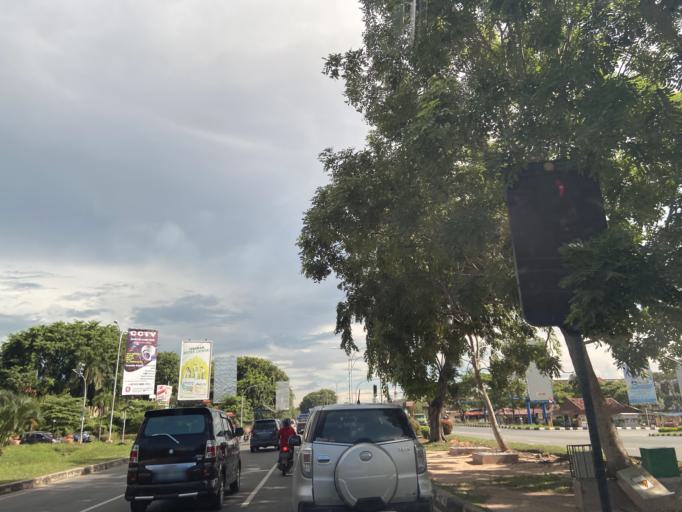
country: SG
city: Singapore
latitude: 1.1114
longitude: 104.0423
